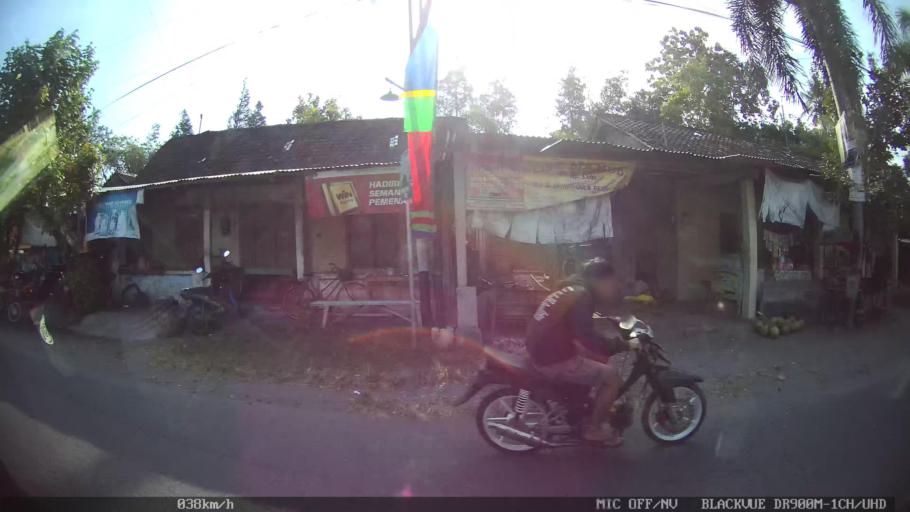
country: ID
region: Daerah Istimewa Yogyakarta
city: Bantul
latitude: -7.8722
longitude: 110.3164
